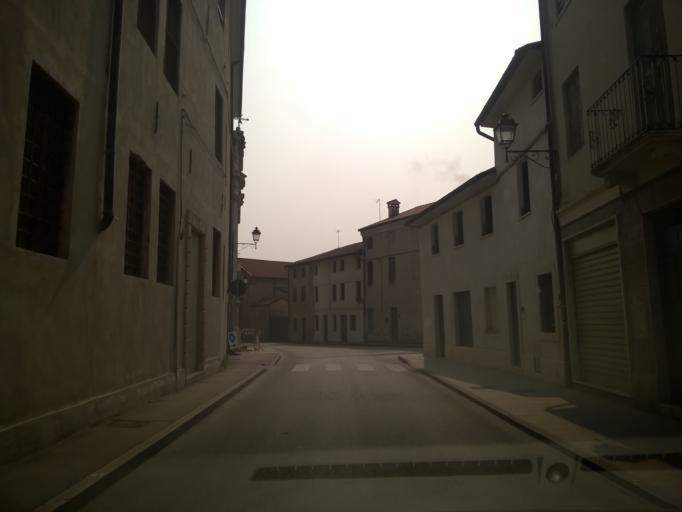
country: IT
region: Veneto
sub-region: Provincia di Vicenza
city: Thiene
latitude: 45.7013
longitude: 11.4806
